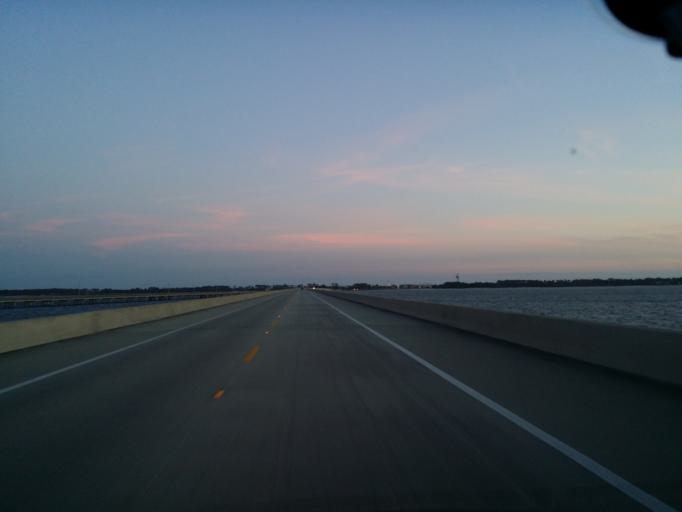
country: US
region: Florida
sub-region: Franklin County
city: Eastpoint
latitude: 29.6784
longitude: -84.8747
